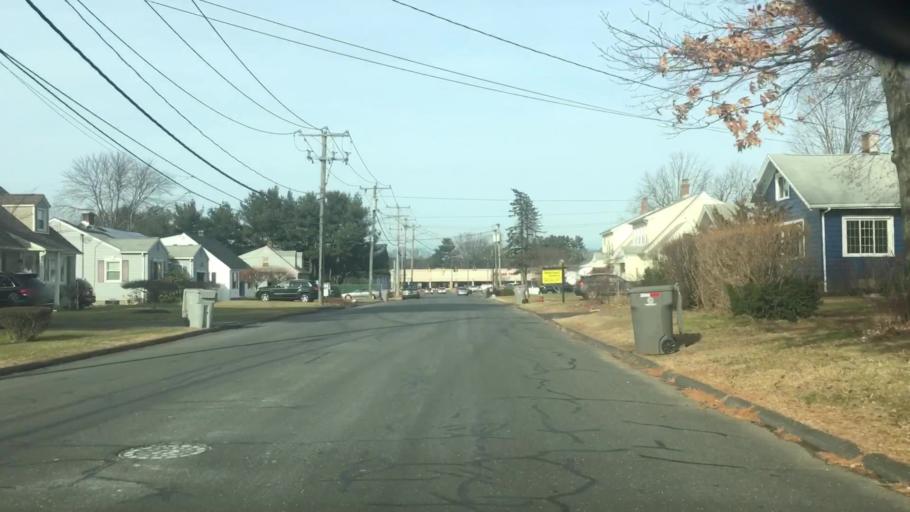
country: US
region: Connecticut
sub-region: Hartford County
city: Bristol
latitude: 41.6890
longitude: -72.9223
